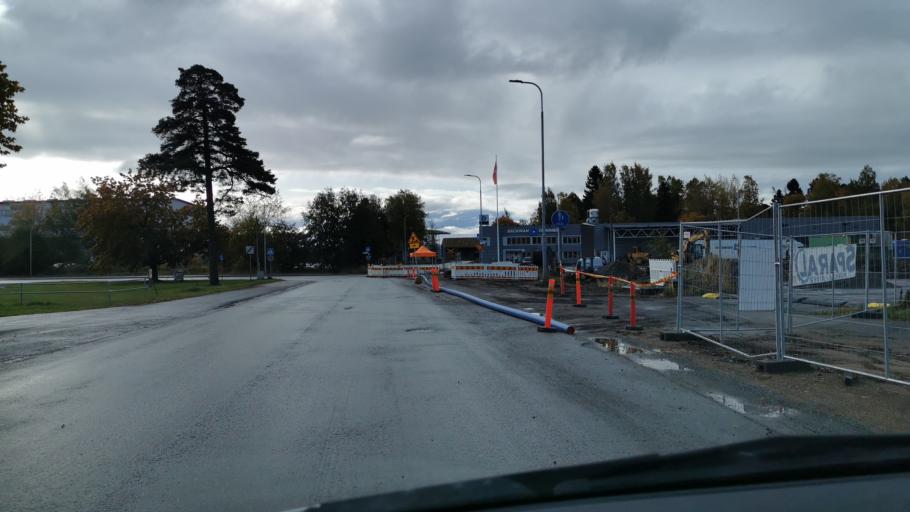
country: FI
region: Ostrobothnia
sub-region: Vaasa
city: Vaasa
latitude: 63.0902
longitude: 21.5639
